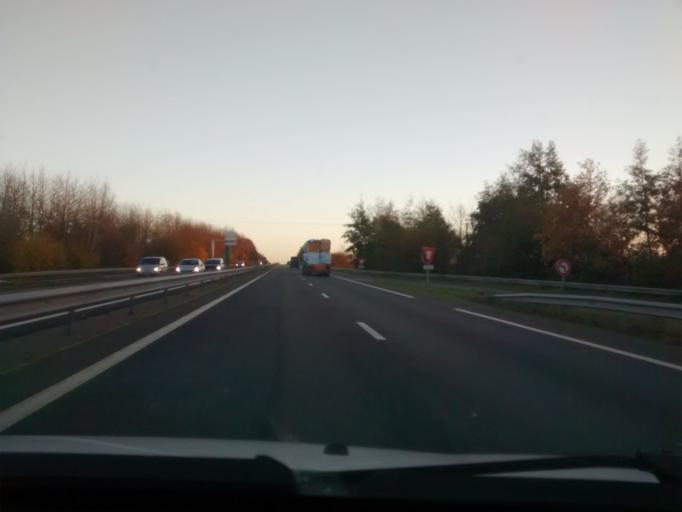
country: FR
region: Brittany
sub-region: Departement d'Ille-et-Vilaine
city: Tinteniac
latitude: 48.3239
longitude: -1.8505
